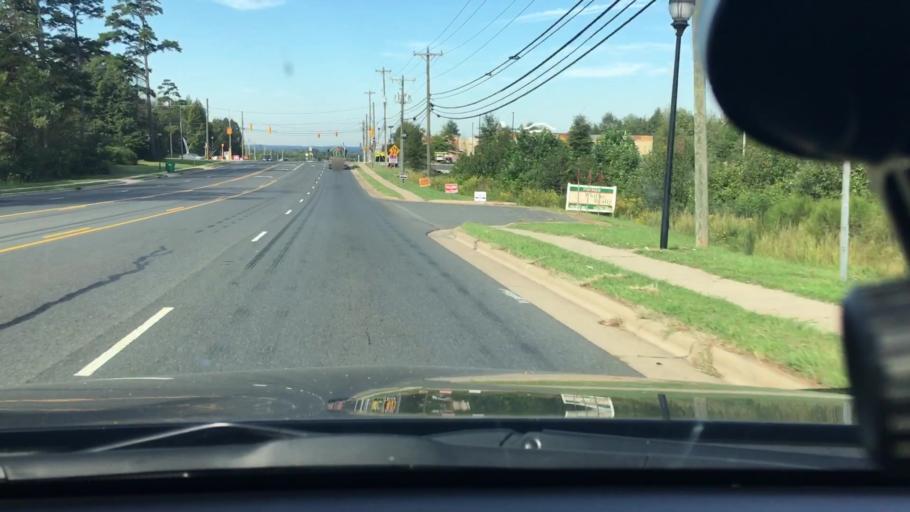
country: US
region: North Carolina
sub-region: Stanly County
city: Locust
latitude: 35.2546
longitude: -80.4493
